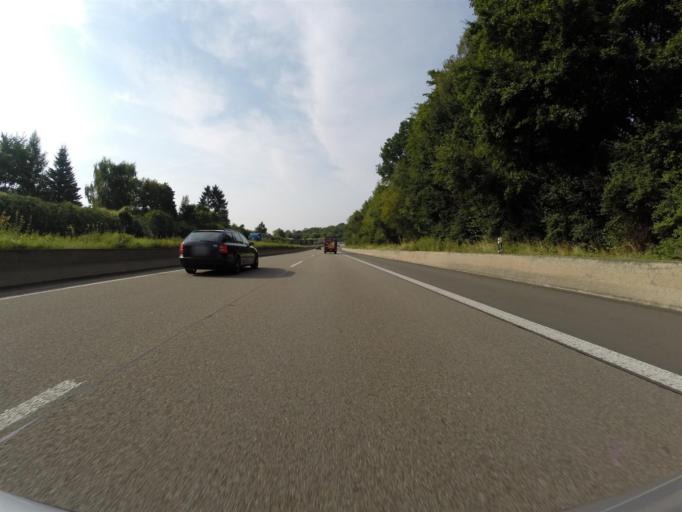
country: DE
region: Thuringia
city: Gerstungen
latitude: 50.9666
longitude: 10.0601
